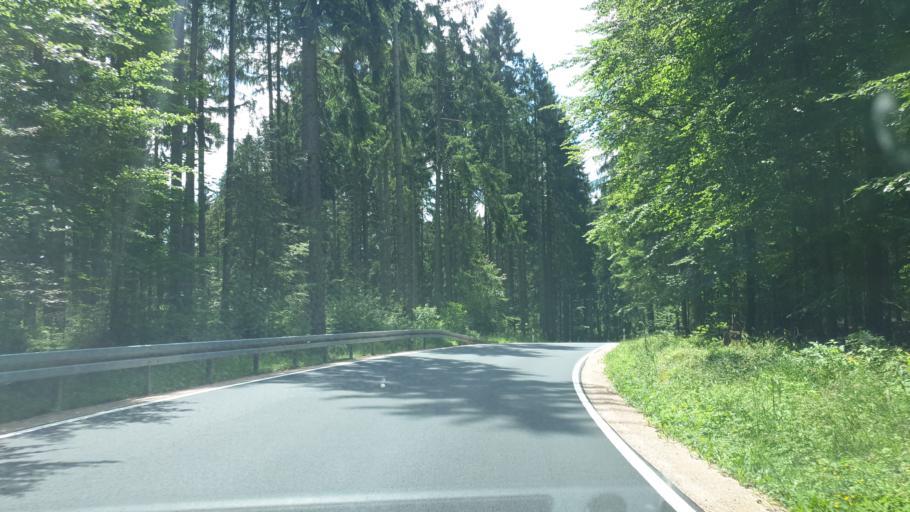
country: DE
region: Saxony
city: Breitenbrunn
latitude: 50.5122
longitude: 12.7429
